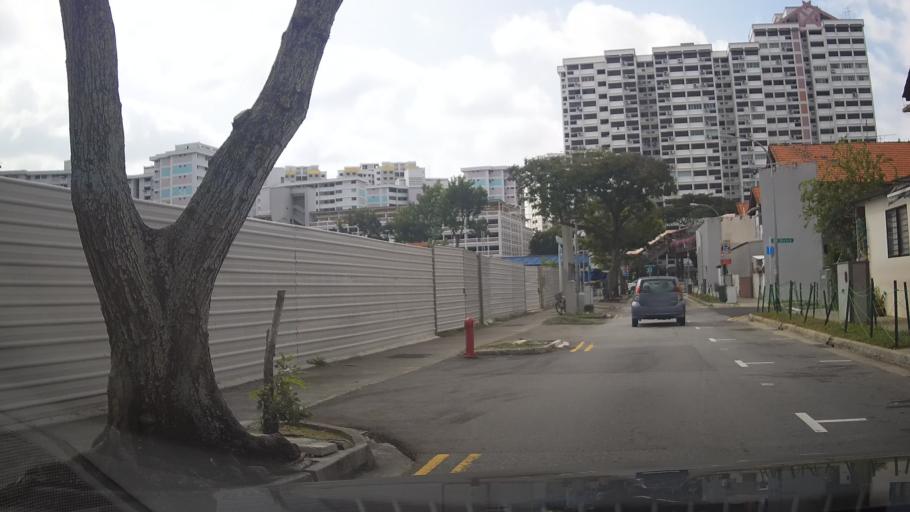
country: SG
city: Singapore
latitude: 1.3119
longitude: 103.8833
